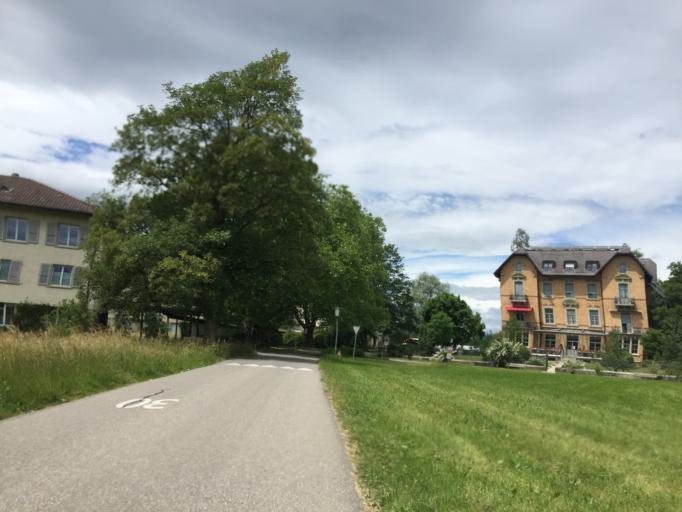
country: CH
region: Bern
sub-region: Bern-Mittelland District
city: Munsingen
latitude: 46.8786
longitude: 7.5534
